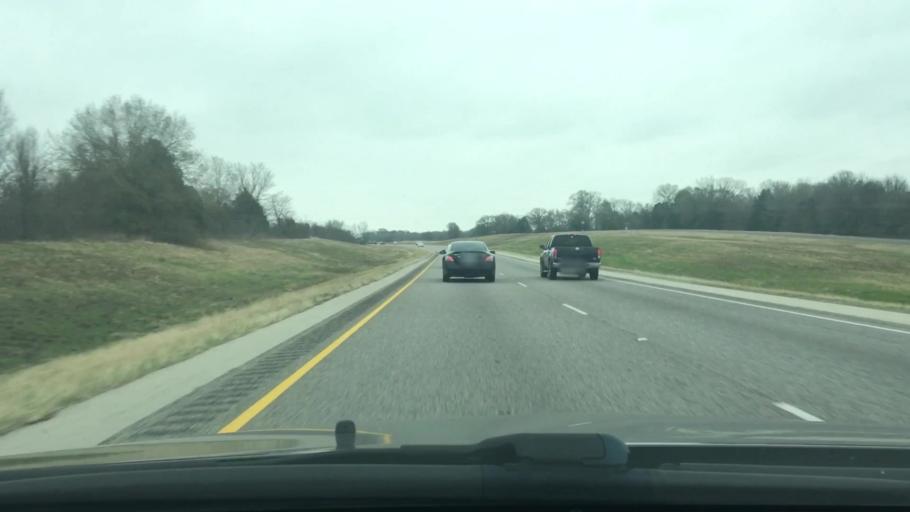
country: US
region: Texas
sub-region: Freestone County
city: Fairfield
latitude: 31.7933
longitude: -96.2511
